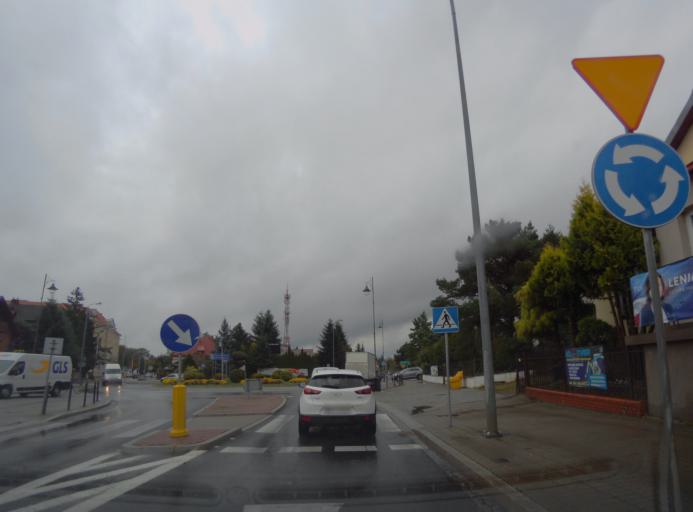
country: PL
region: Subcarpathian Voivodeship
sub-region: Powiat lezajski
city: Lezajsk
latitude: 50.2570
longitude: 22.4216
